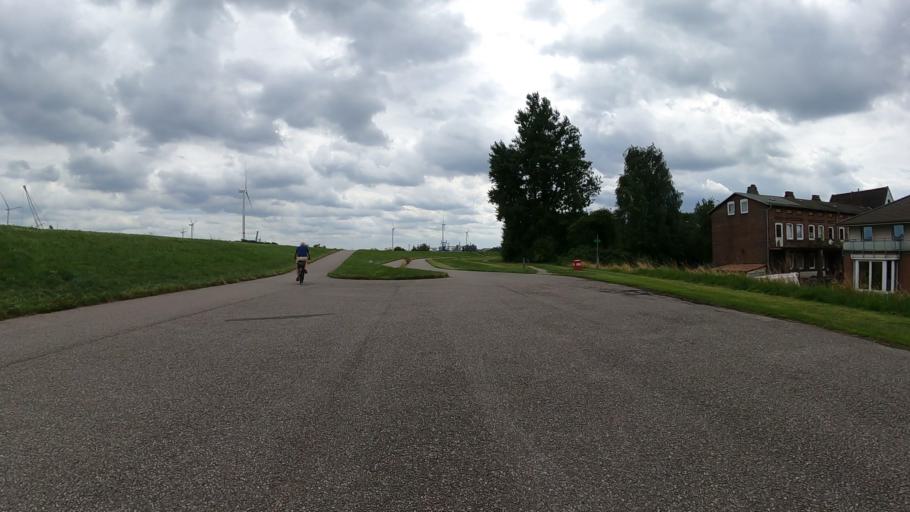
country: DE
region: Hamburg
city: Altona
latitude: 53.5282
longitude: 9.8876
